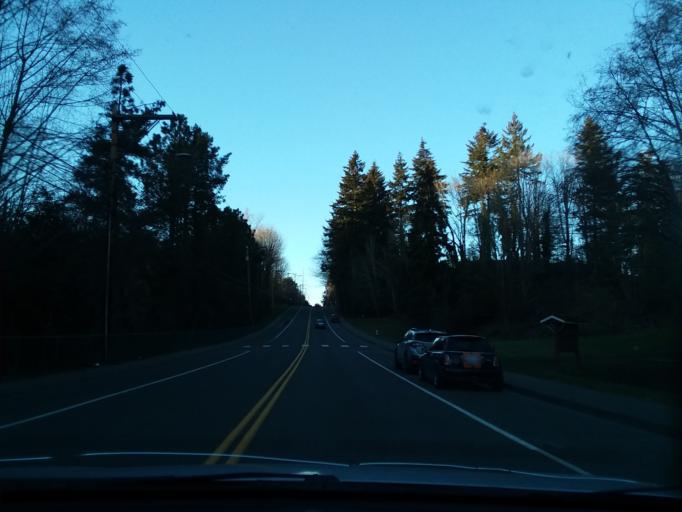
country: US
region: Washington
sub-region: Snohomish County
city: Mountlake Terrace
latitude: 47.7888
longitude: -122.2976
